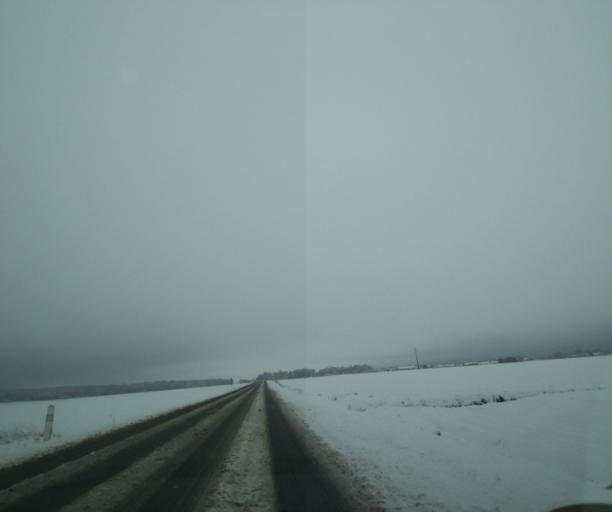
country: FR
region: Champagne-Ardenne
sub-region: Departement de la Haute-Marne
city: Wassy
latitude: 48.5581
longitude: 4.9254
